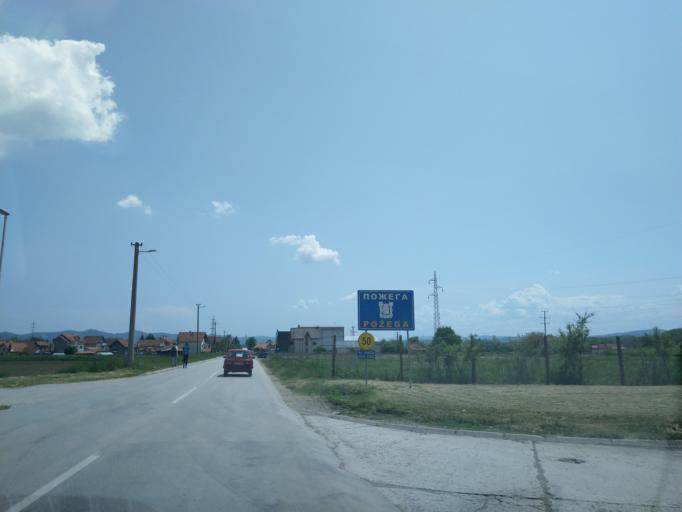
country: RS
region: Central Serbia
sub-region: Zlatiborski Okrug
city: Pozega
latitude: 43.8486
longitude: 20.0123
